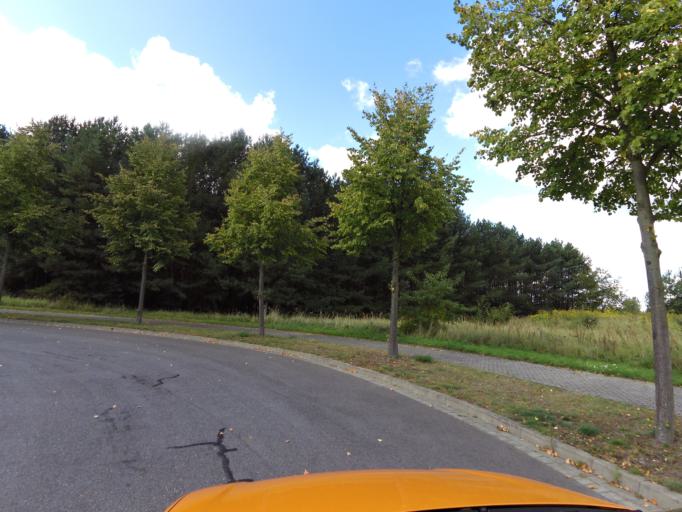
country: DE
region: Brandenburg
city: Luckenwalde
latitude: 52.0921
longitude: 13.1305
